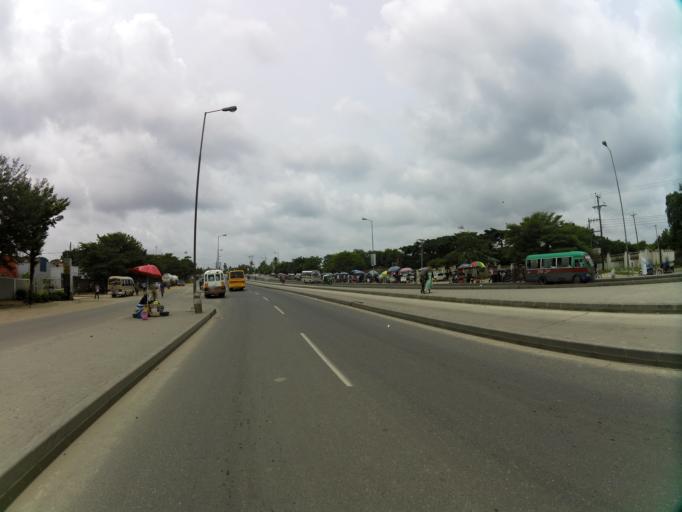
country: TZ
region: Dar es Salaam
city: Magomeni
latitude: -6.7915
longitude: 39.2048
